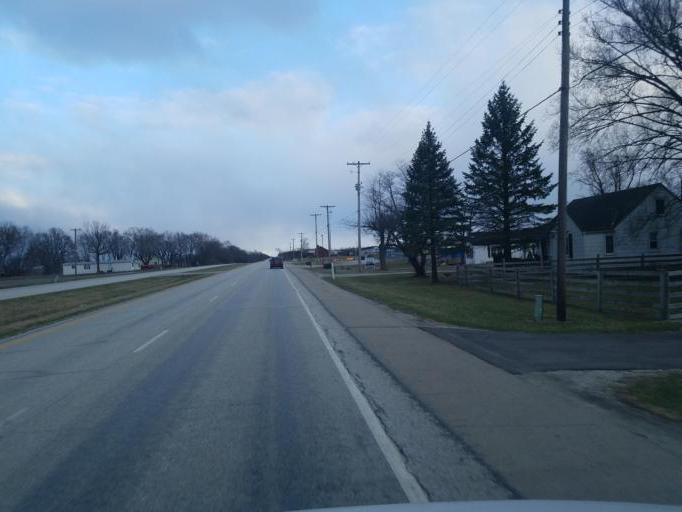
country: US
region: Indiana
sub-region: Hancock County
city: Greenfield
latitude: 39.7872
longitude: -85.7243
